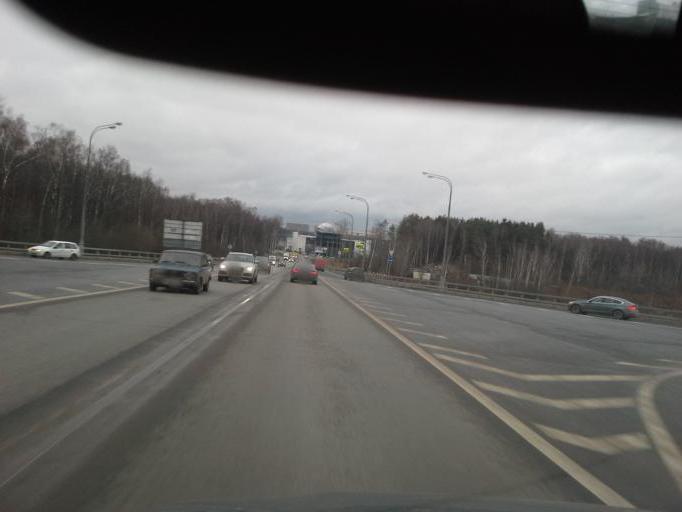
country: RU
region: Moskovskaya
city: Moskovskiy
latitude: 55.6099
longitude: 37.3514
